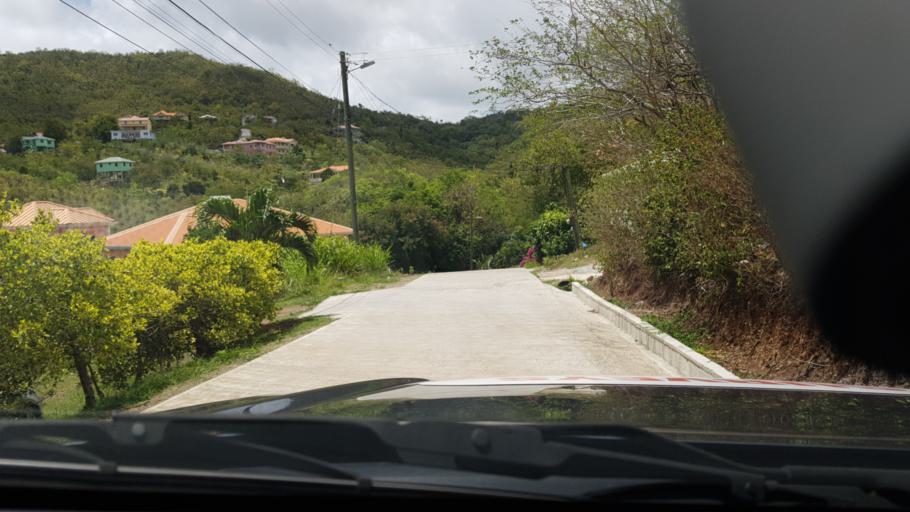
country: LC
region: Gros-Islet
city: Gros Islet
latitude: 14.0673
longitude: -60.9330
